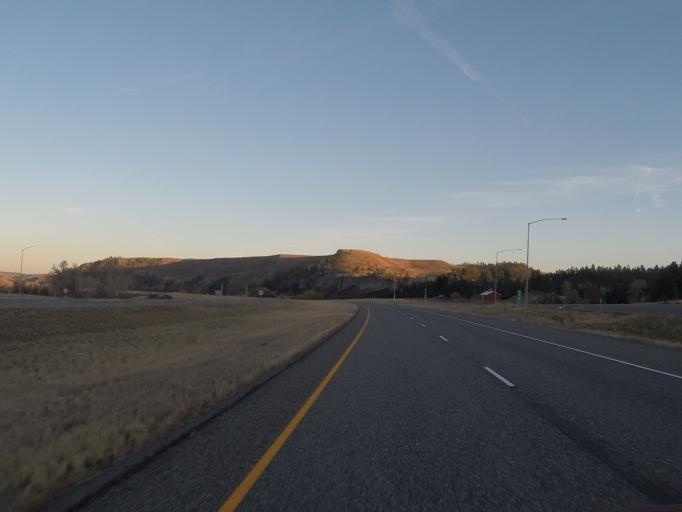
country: US
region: Montana
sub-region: Sweet Grass County
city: Big Timber
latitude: 45.7353
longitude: -109.7578
